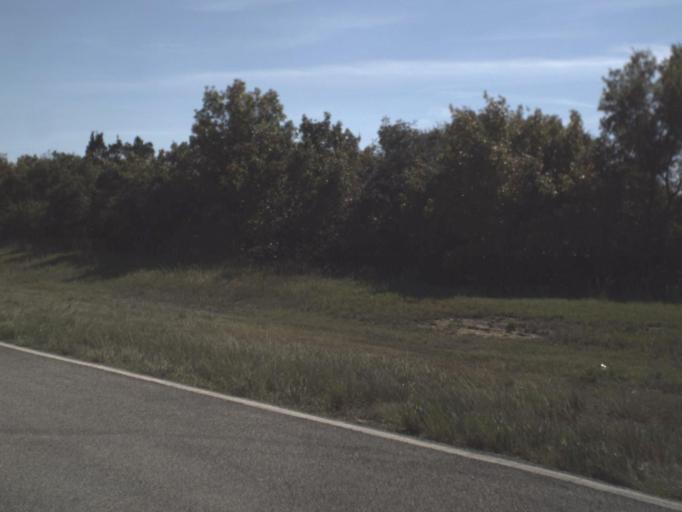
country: US
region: Florida
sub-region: Highlands County
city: Lake Placid
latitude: 27.2752
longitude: -81.3523
